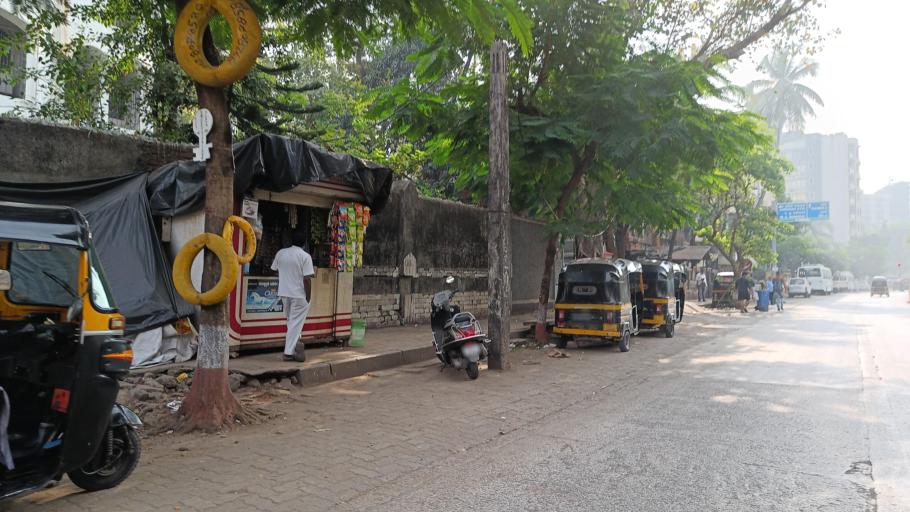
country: IN
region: Maharashtra
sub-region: Mumbai Suburban
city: Mumbai
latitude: 19.1140
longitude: 72.8367
